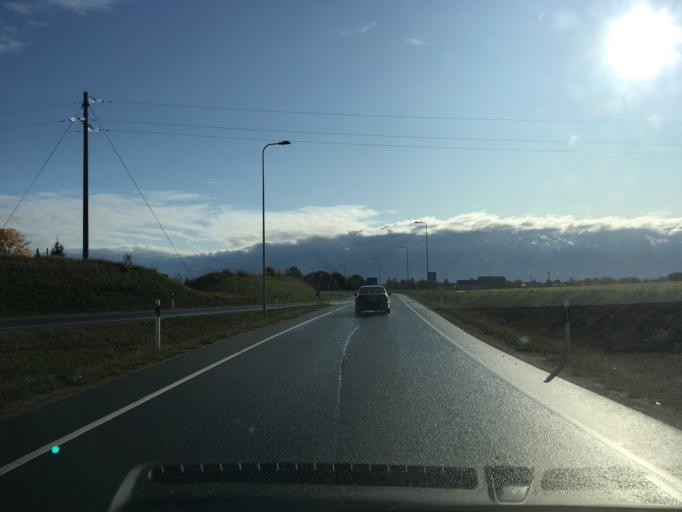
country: EE
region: Harju
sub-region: Rae vald
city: Vaida
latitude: 59.1826
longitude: 25.1114
